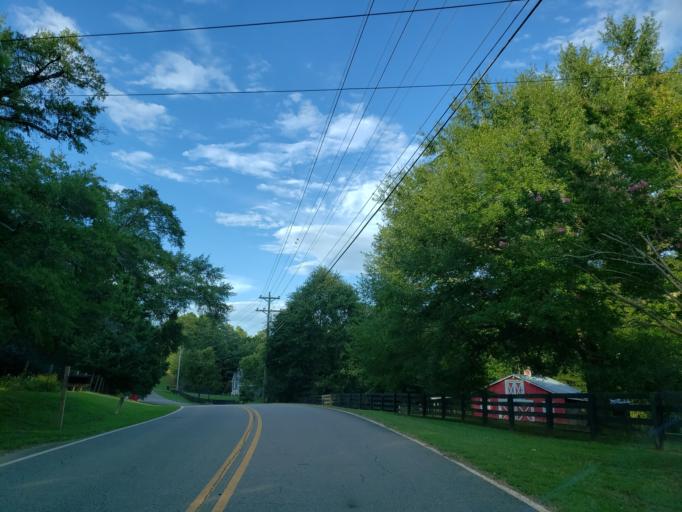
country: US
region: Georgia
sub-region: Cherokee County
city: Canton
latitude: 34.3213
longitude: -84.5200
